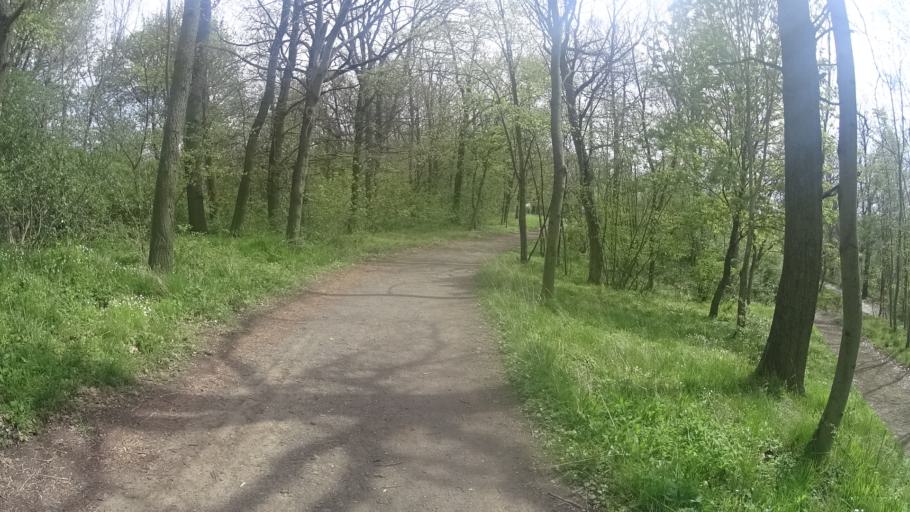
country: DE
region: Thuringia
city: Wandersleben
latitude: 50.8671
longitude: 10.8357
